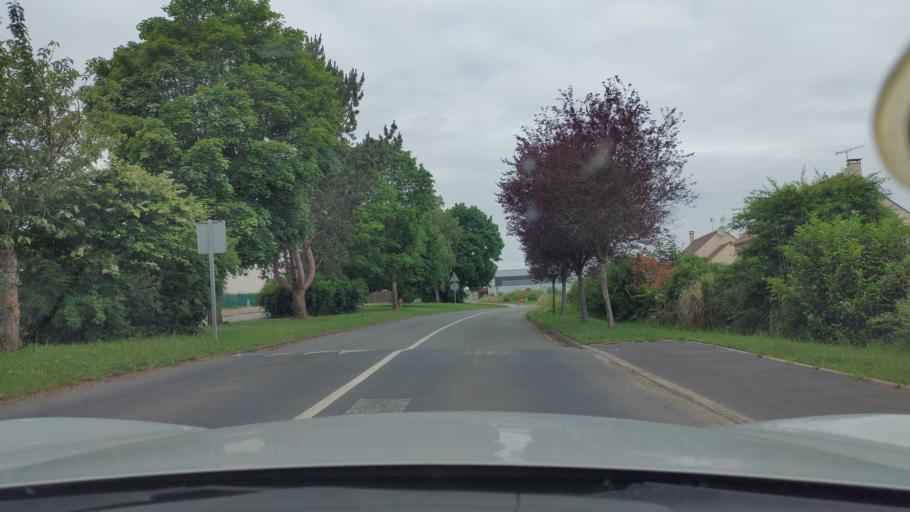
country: FR
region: Picardie
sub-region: Departement de l'Oise
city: Betz
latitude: 49.1593
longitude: 2.9497
